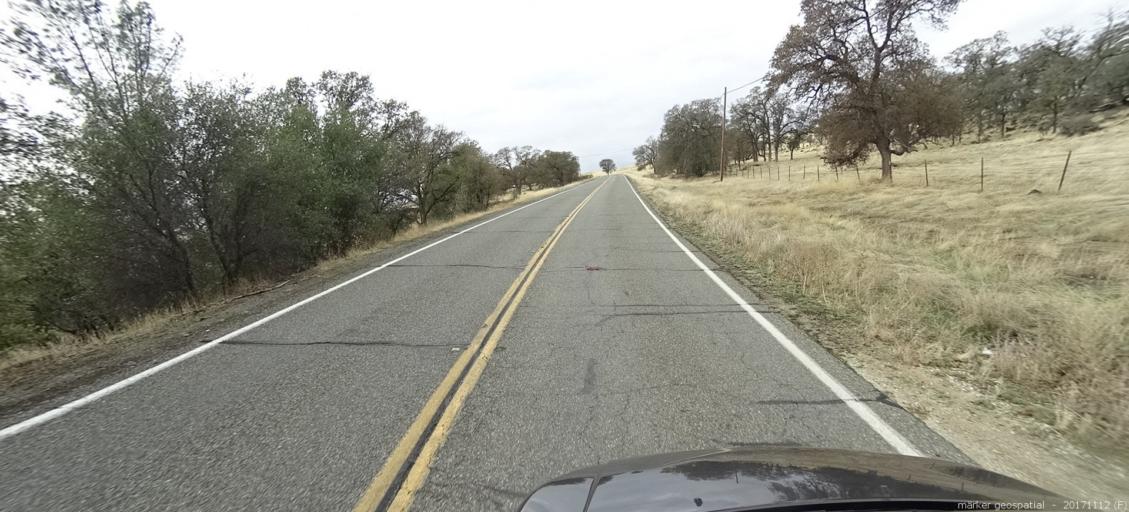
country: US
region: California
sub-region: Shasta County
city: Palo Cedro
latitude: 40.4845
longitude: -122.1560
